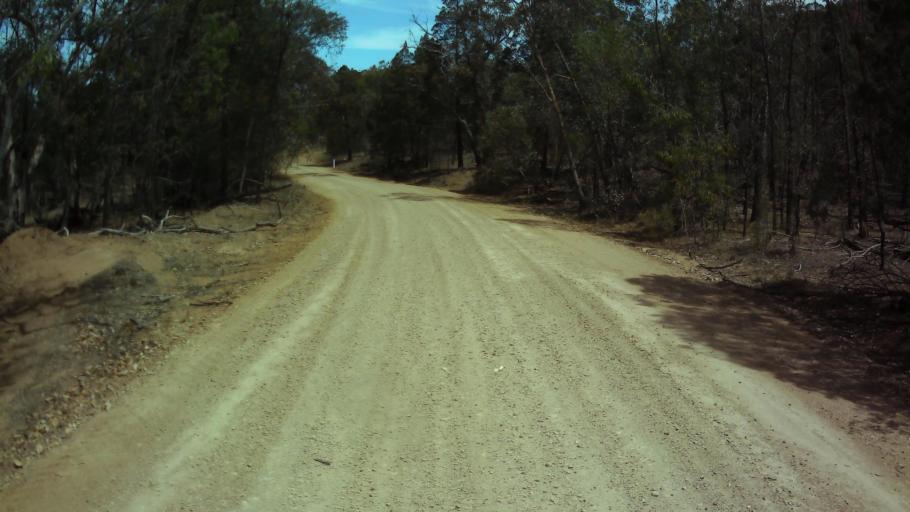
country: AU
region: New South Wales
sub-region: Weddin
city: Grenfell
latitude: -33.8158
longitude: 148.1649
